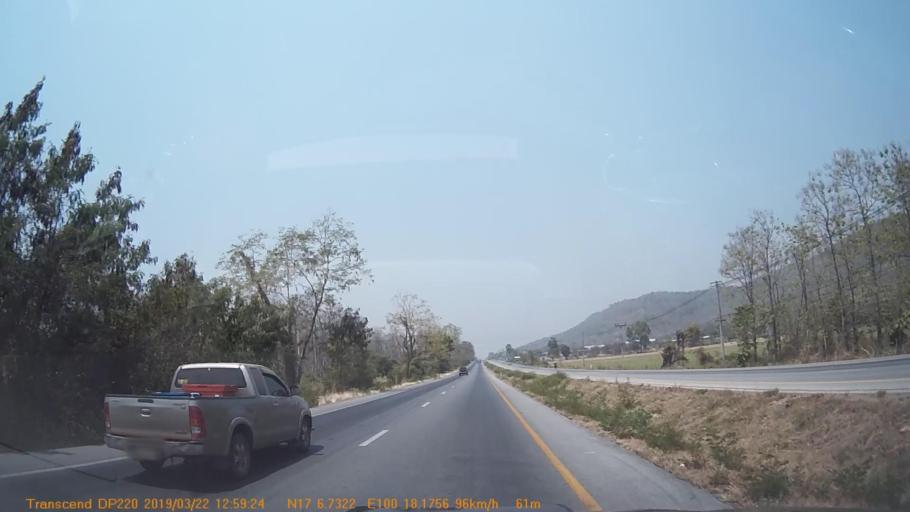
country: TH
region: Phitsanulok
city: Phrom Phiram
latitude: 17.1126
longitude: 100.3027
